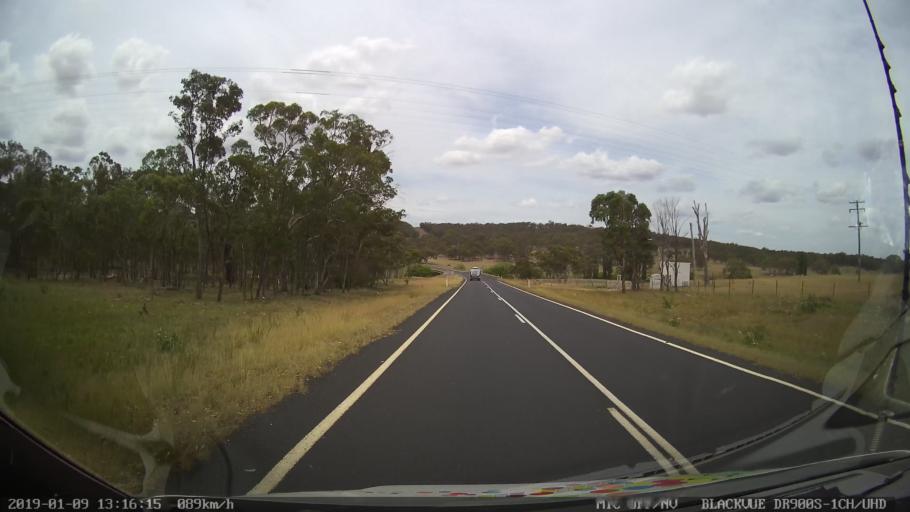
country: AU
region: New South Wales
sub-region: Armidale Dumaresq
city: Armidale
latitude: -30.5450
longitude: 151.7938
